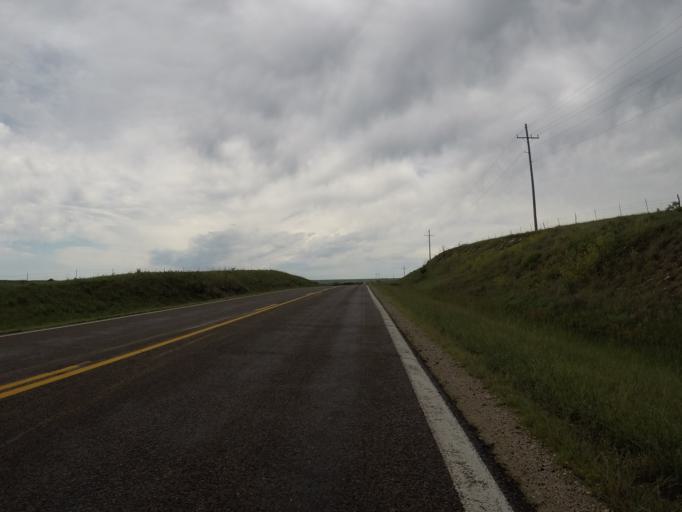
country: US
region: Kansas
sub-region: Wabaunsee County
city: Alma
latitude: 38.8700
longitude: -96.1451
